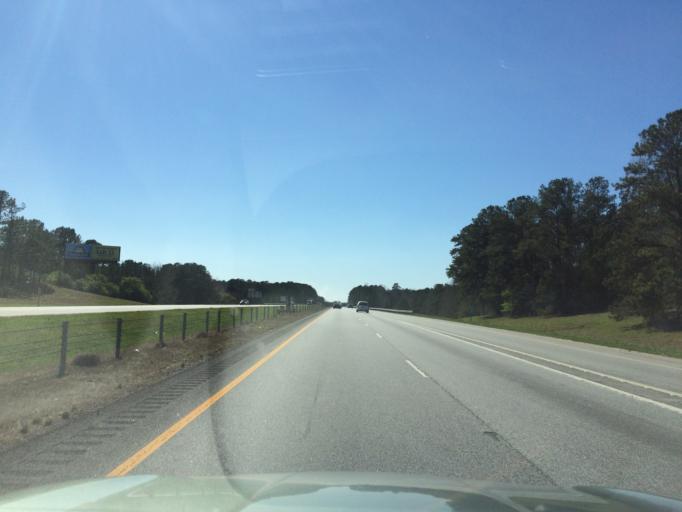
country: US
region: Alabama
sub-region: Macon County
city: Tuskegee
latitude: 32.4856
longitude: -85.6401
